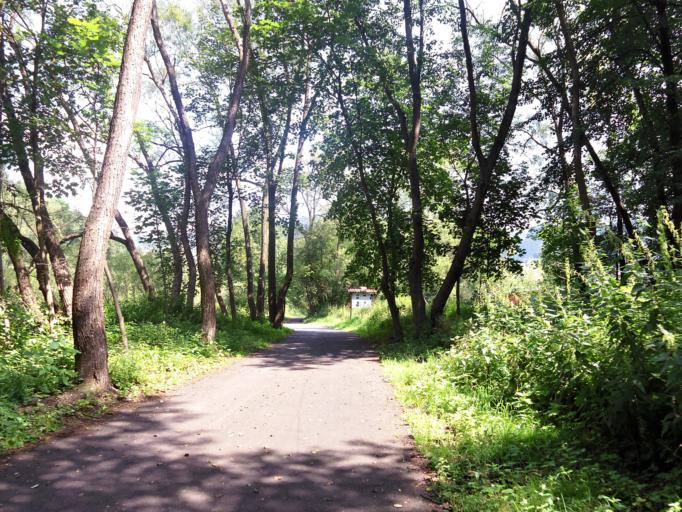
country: PL
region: Silesian Voivodeship
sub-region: Powiat zywiecki
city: Rajcza
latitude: 49.5094
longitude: 19.1118
